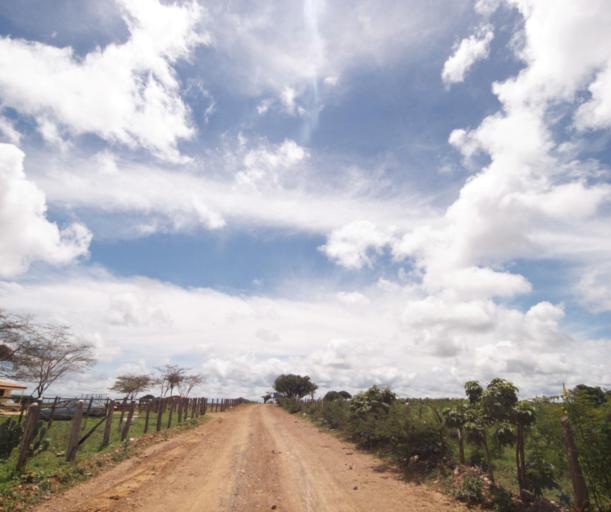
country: BR
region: Bahia
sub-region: Tanhacu
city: Tanhacu
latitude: -14.1912
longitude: -41.0658
